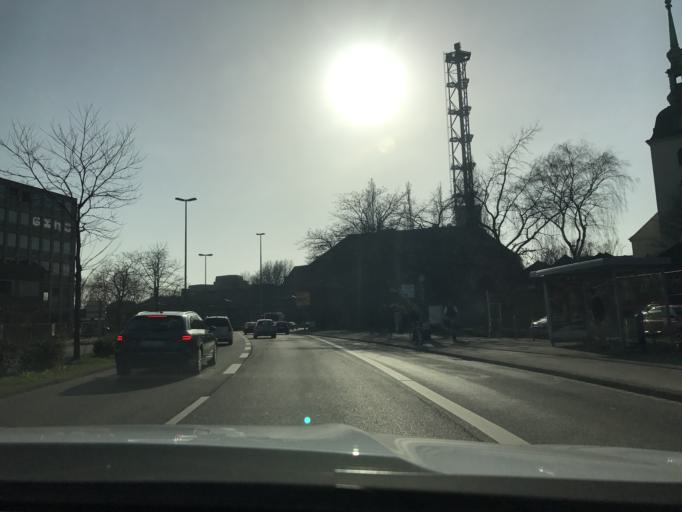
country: DE
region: North Rhine-Westphalia
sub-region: Regierungsbezirk Dusseldorf
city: Duisburg
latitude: 51.4315
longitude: 6.7582
